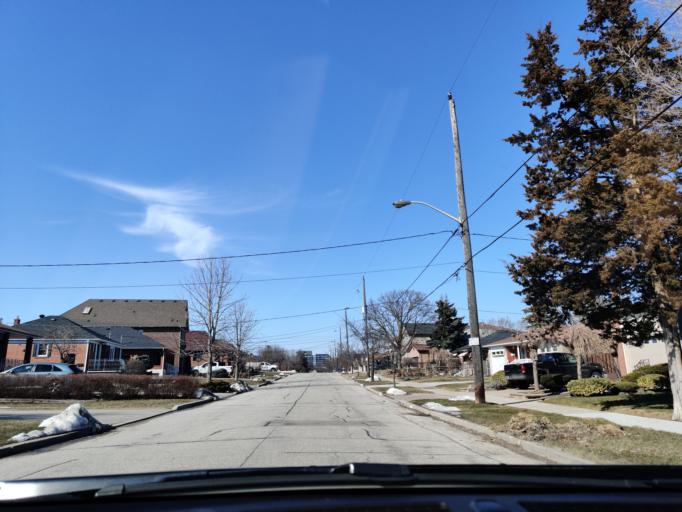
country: CA
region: Ontario
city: Toronto
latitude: 43.7190
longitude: -79.4777
